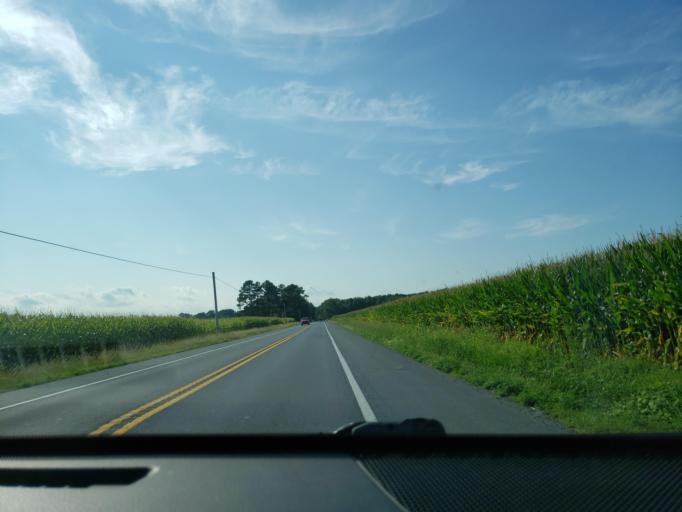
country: US
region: Delaware
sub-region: Sussex County
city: Milton
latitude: 38.7563
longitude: -75.2578
